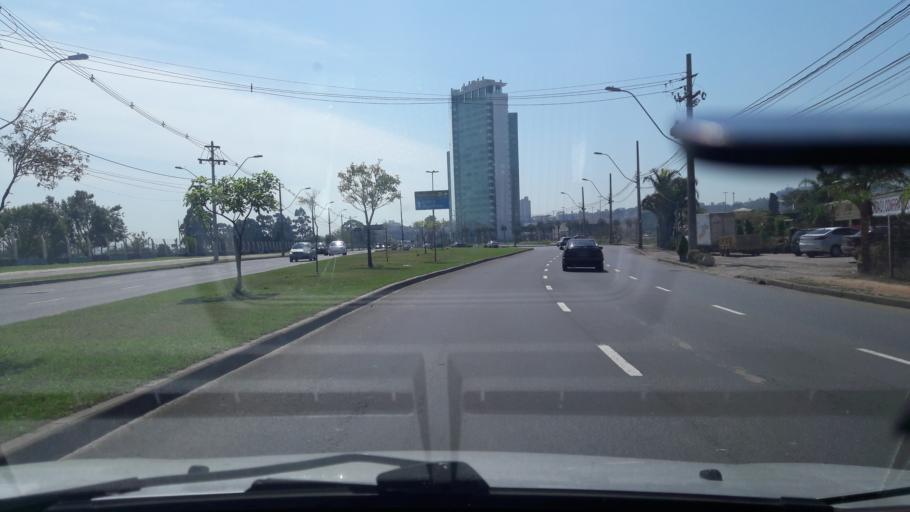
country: BR
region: Rio Grande do Sul
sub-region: Porto Alegre
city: Porto Alegre
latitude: -30.0900
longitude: -51.2486
